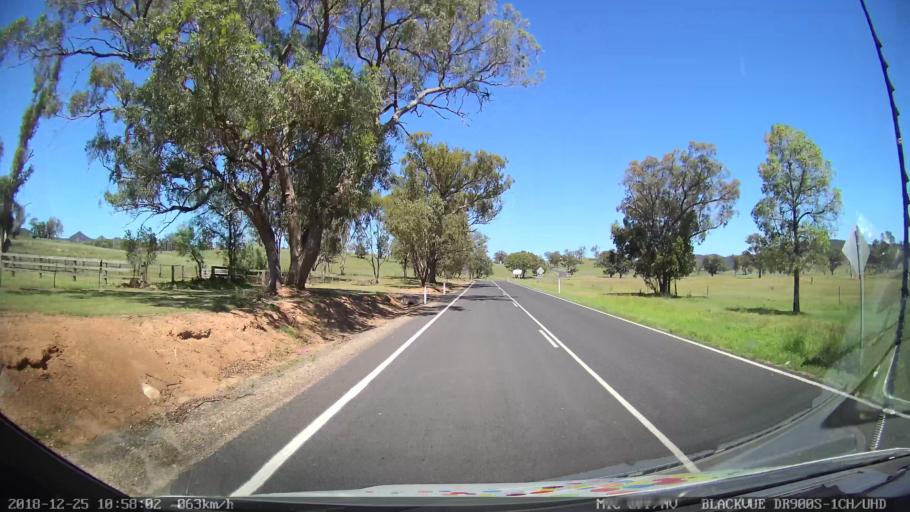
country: AU
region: New South Wales
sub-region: Upper Hunter Shire
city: Merriwa
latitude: -32.4047
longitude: 150.2443
